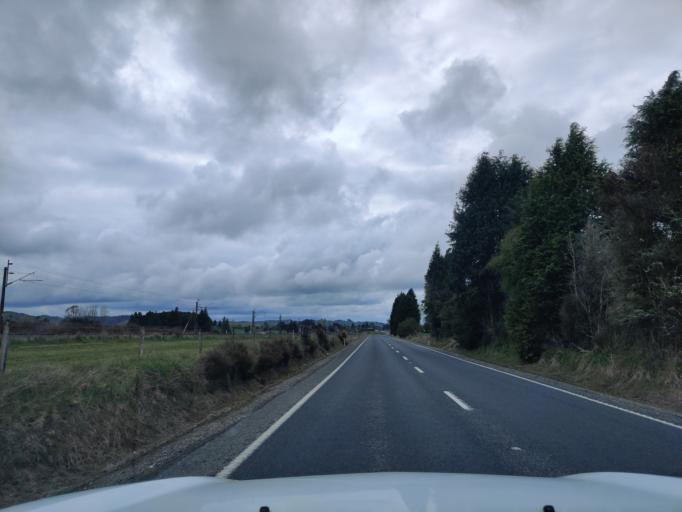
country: NZ
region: Waikato
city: Turangi
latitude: -39.0160
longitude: 175.3786
